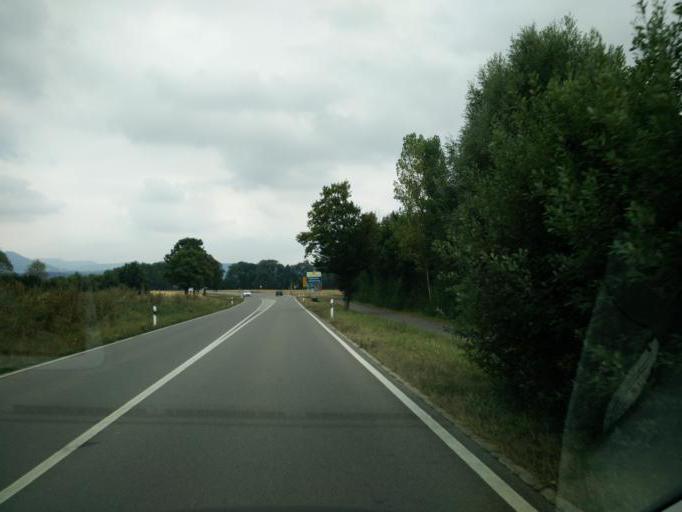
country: DE
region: Baden-Wuerttemberg
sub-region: Tuebingen Region
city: Dusslingen
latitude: 48.4626
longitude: 9.0731
